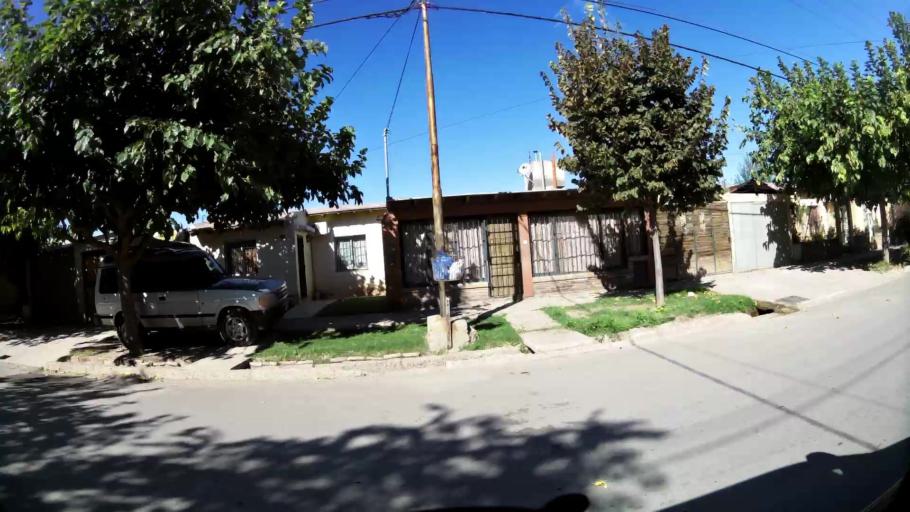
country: AR
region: Mendoza
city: Las Heras
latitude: -32.8489
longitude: -68.8238
